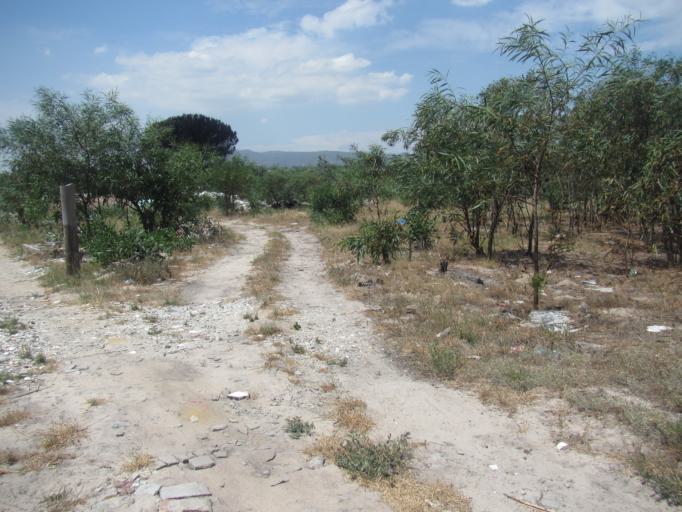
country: ZA
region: Western Cape
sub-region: Cape Winelands District Municipality
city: Stellenbosch
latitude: -33.8053
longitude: 18.8546
